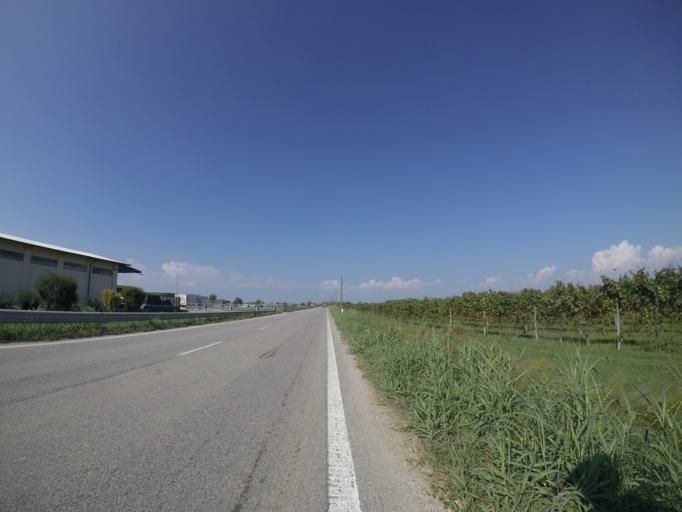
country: IT
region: Friuli Venezia Giulia
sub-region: Provincia di Udine
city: Carlino
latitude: 45.7957
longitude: 13.1658
